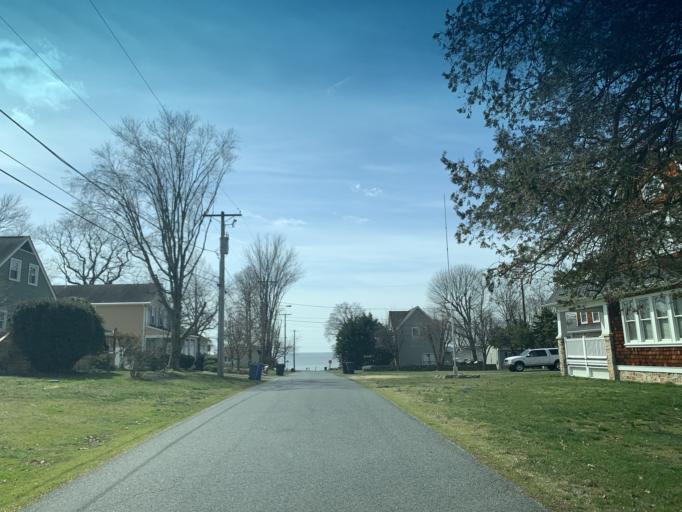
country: US
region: Maryland
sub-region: Cecil County
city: Charlestown
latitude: 39.5725
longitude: -75.9743
